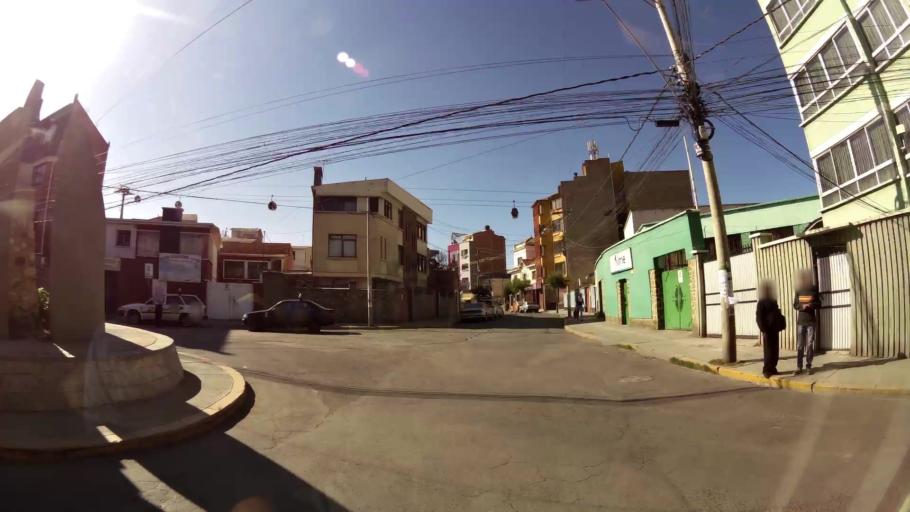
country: BO
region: La Paz
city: La Paz
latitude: -16.5167
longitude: -68.1274
